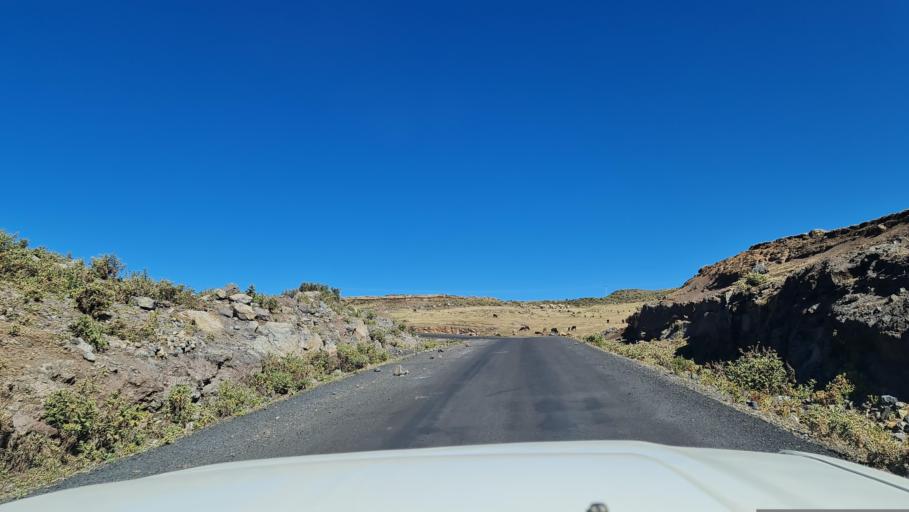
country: ET
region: Amhara
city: Debark'
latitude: 13.1375
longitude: 38.1780
